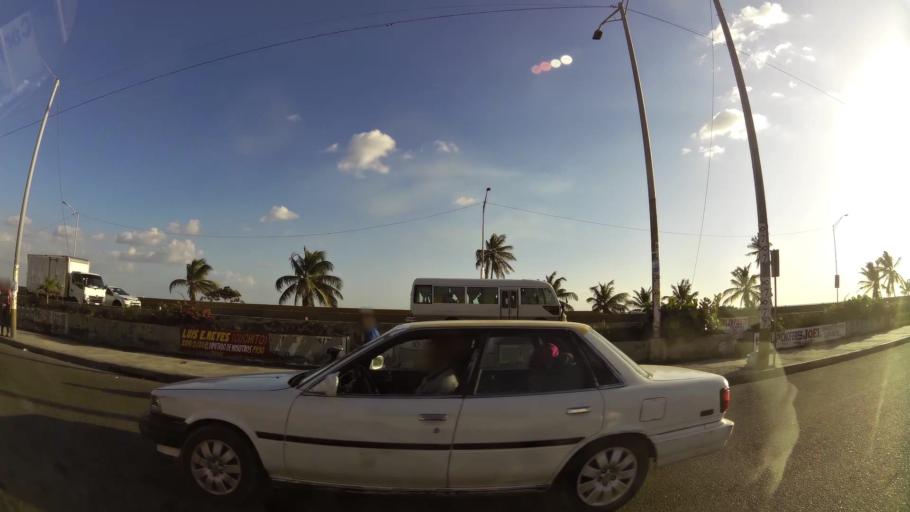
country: DO
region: Santo Domingo
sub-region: Santo Domingo
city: Santo Domingo Este
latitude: 18.4655
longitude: -69.8191
